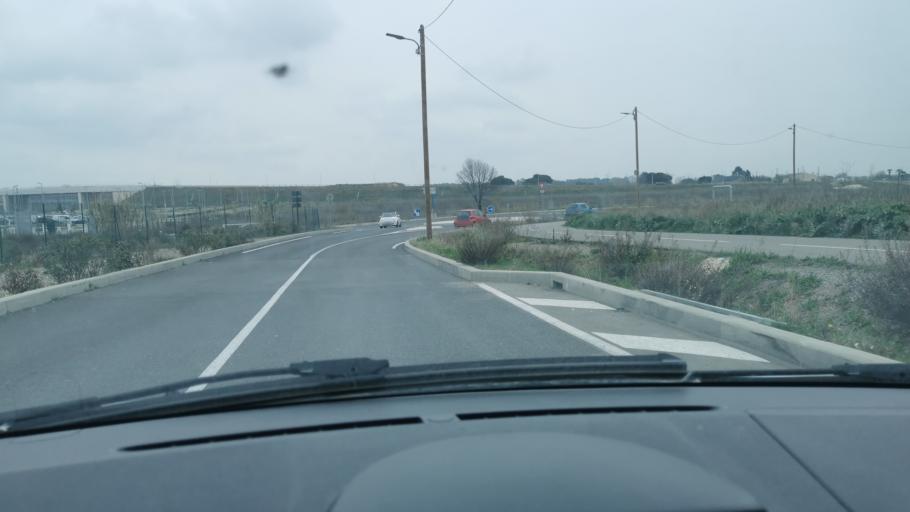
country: FR
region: Languedoc-Roussillon
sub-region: Departement de l'Herault
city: Lattes
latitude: 43.5946
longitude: 3.9259
